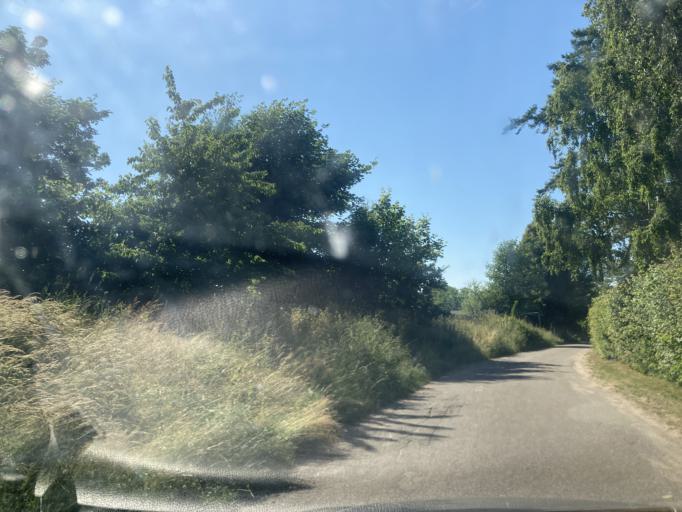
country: DK
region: Capital Region
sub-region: Halsnaes Kommune
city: Liseleje
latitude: 56.0053
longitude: 11.9687
